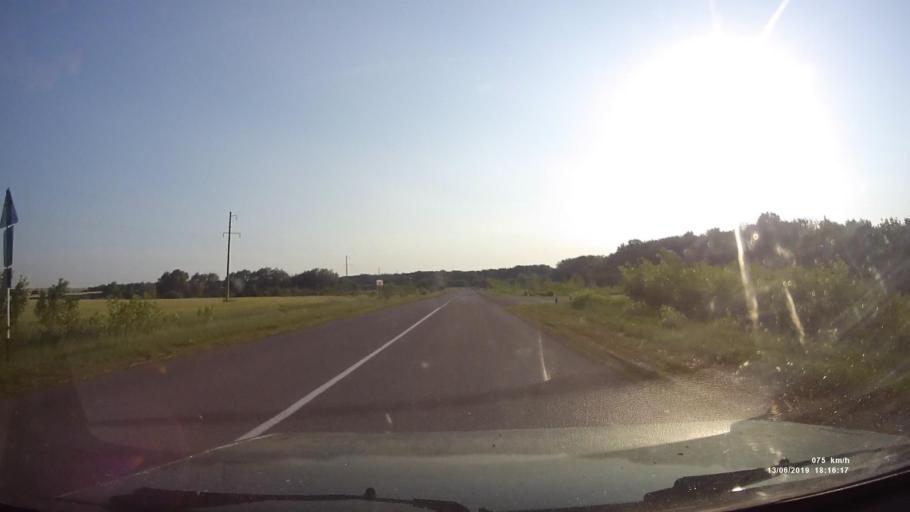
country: RU
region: Rostov
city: Kazanskaya
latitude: 49.9278
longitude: 41.3418
